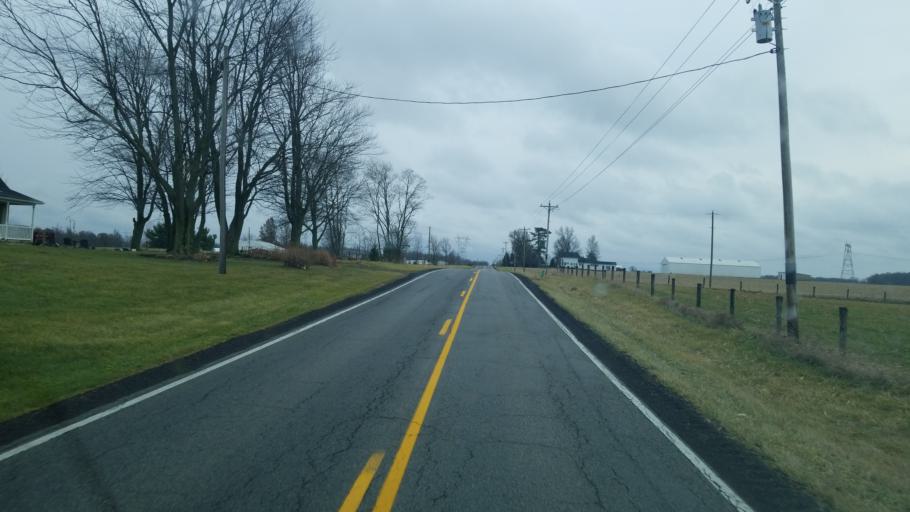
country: US
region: Ohio
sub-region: Union County
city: Marysville
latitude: 40.3068
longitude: -83.3525
